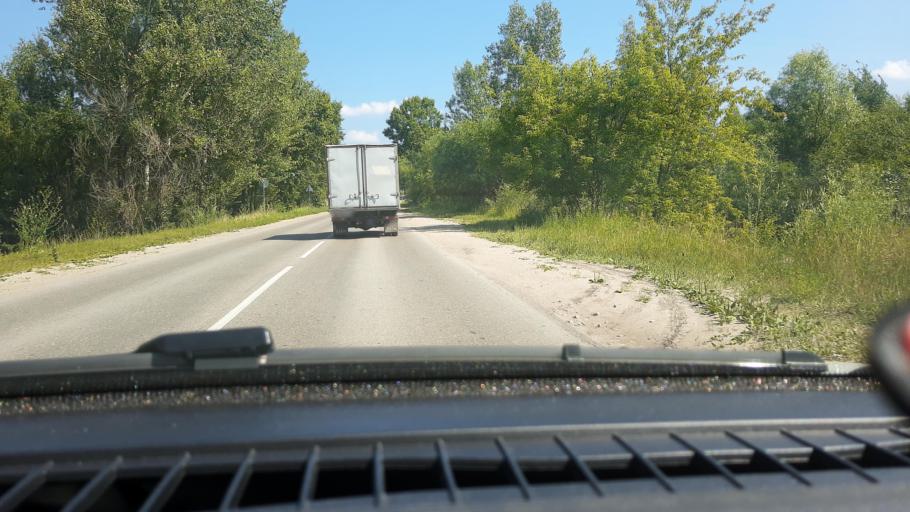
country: RU
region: Nizjnij Novgorod
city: Afonino
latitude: 56.2955
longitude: 44.1890
